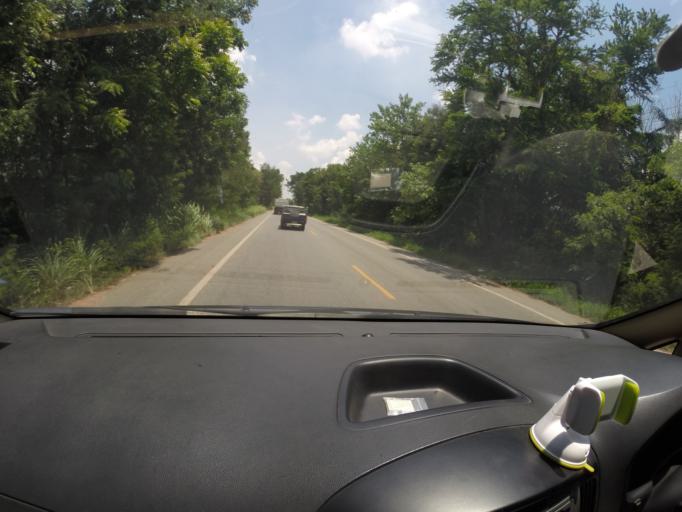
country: TH
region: Nakhon Ratchasima
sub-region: Amphoe Thepharak
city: Thepharak
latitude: 15.1279
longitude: 101.5583
